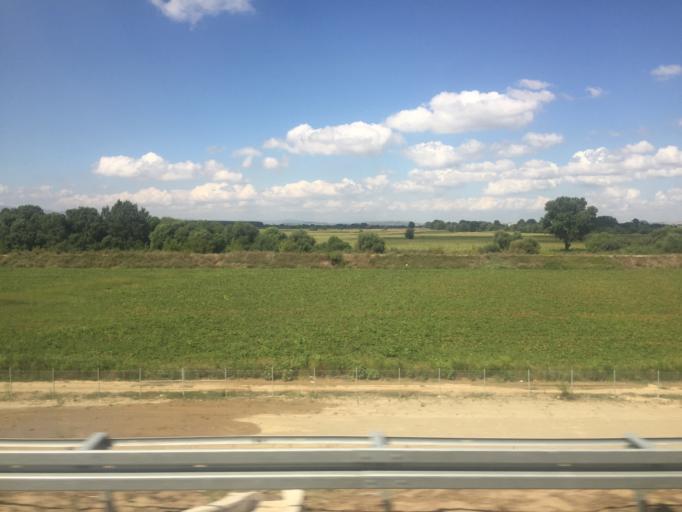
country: TR
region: Bursa
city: Tatkavakli
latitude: 40.1038
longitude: 28.2780
